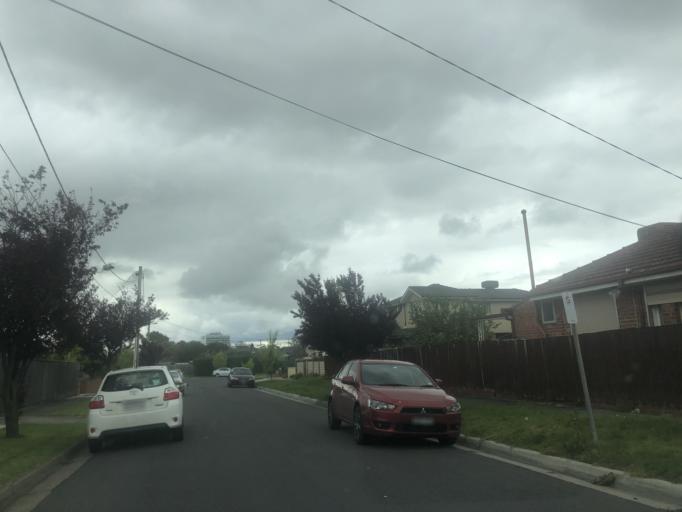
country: AU
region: Victoria
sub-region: Greater Dandenong
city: Dandenong North
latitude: -37.9788
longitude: 145.2145
